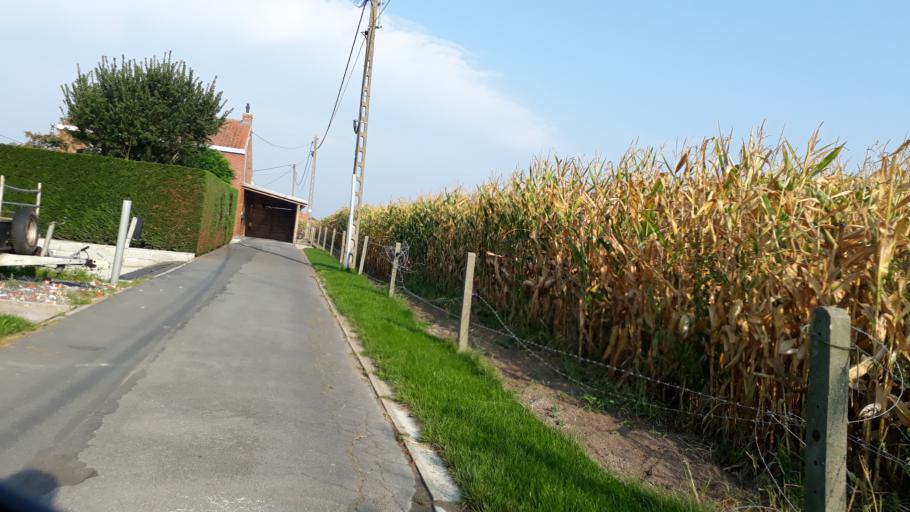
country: BE
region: Flanders
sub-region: Provincie West-Vlaanderen
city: Torhout
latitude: 51.0960
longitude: 3.0690
